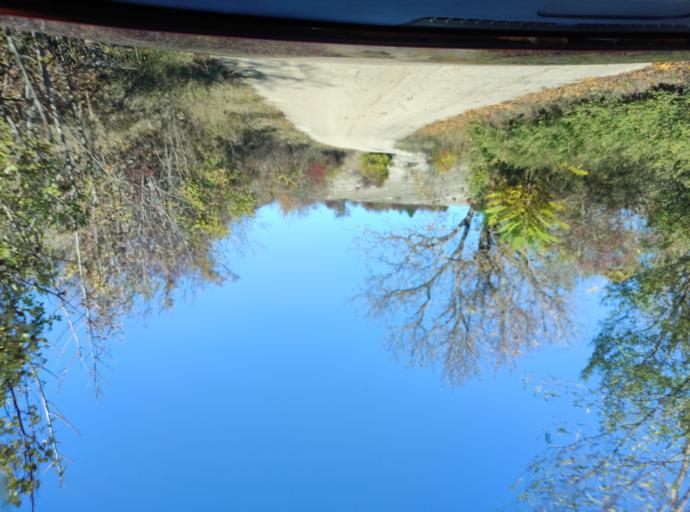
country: BG
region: Montana
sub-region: Obshtina Montana
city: Montana
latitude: 43.4397
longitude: 23.0534
